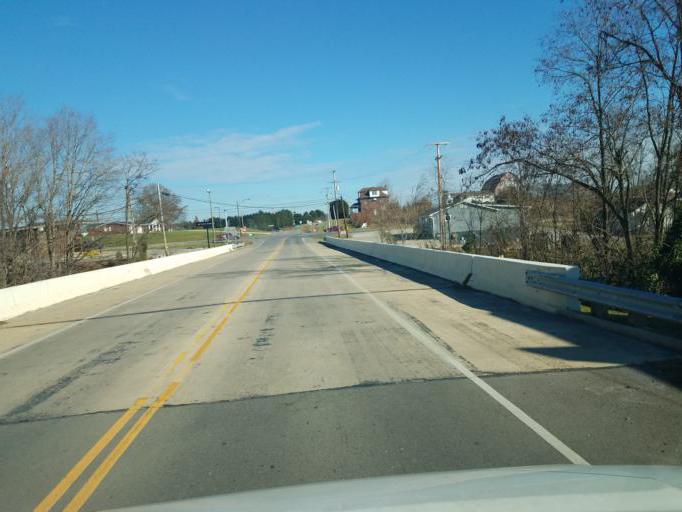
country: US
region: Ohio
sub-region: Scioto County
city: Sciotodale
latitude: 38.8600
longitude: -82.8599
